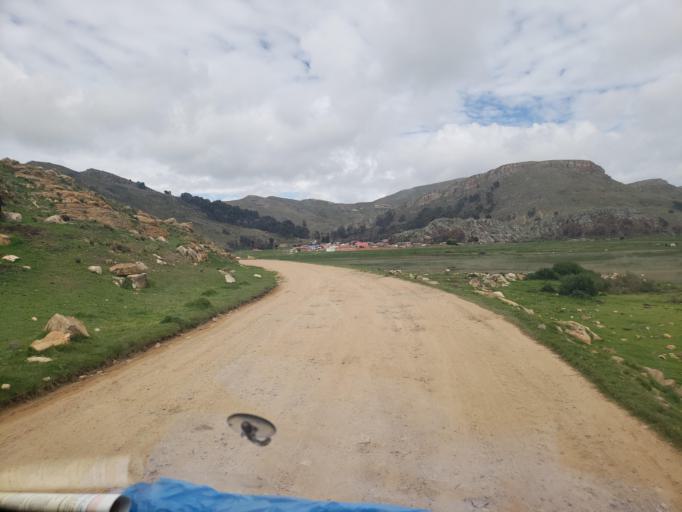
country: BO
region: La Paz
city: Batallas
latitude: -16.3505
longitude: -68.6281
